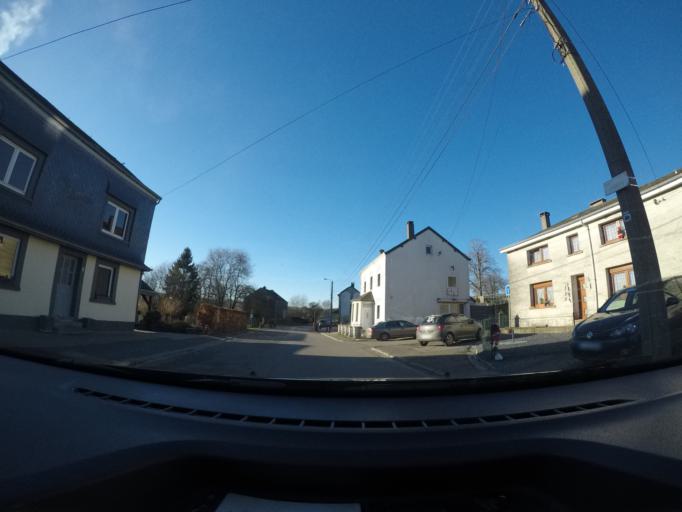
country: BE
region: Wallonia
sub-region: Province du Luxembourg
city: Bertrix
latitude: 49.8348
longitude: 5.3054
